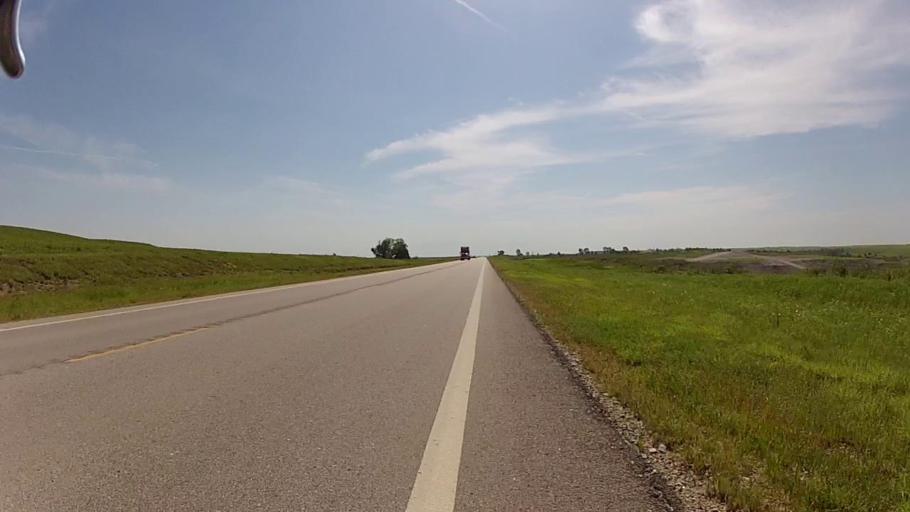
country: US
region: Kansas
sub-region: Cowley County
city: Winfield
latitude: 37.1108
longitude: -96.6236
